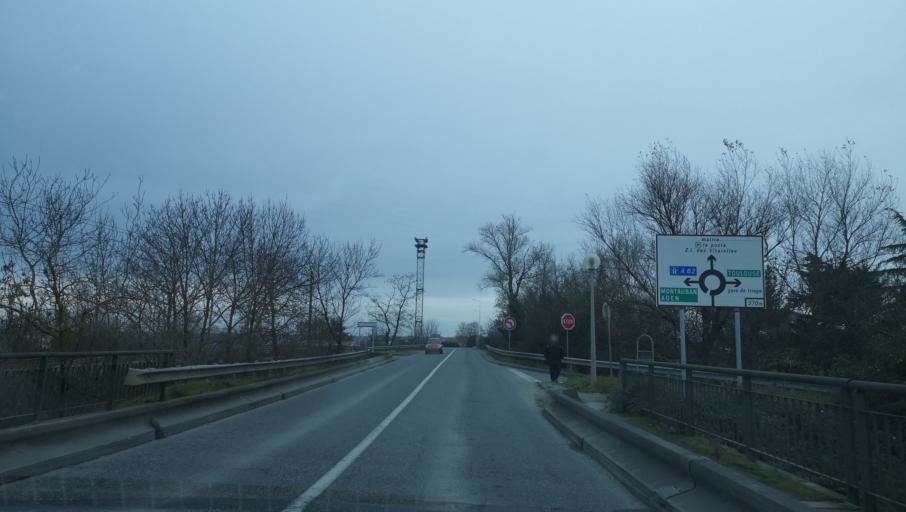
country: FR
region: Midi-Pyrenees
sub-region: Departement de la Haute-Garonne
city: Lespinasse
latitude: 43.7096
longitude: 1.3870
